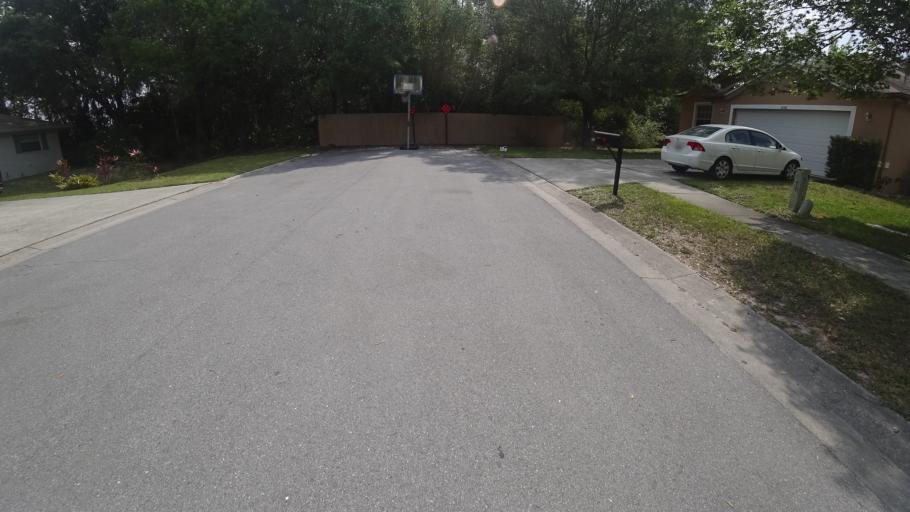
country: US
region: Florida
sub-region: Sarasota County
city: North Sarasota
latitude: 27.4005
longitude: -82.5198
